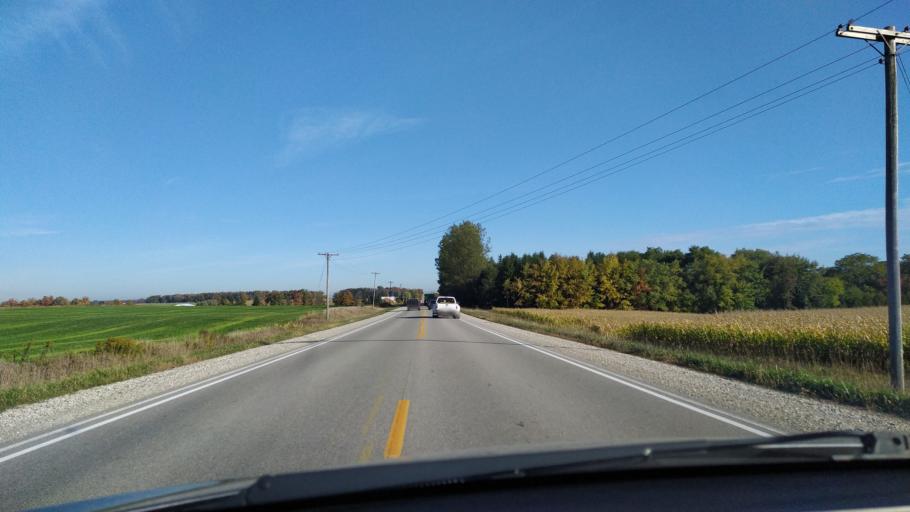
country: CA
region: Ontario
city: Stratford
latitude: 43.4542
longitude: -80.8390
